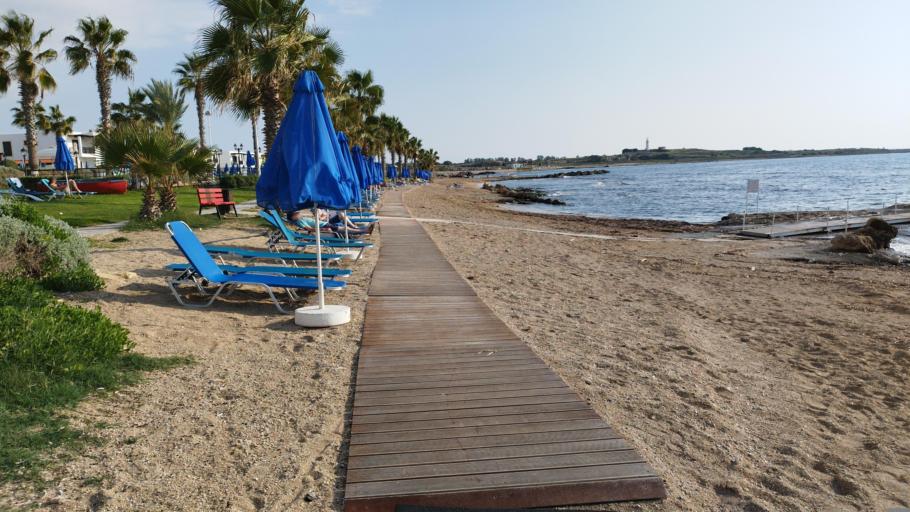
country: CY
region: Pafos
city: Paphos
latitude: 34.7697
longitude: 32.4050
